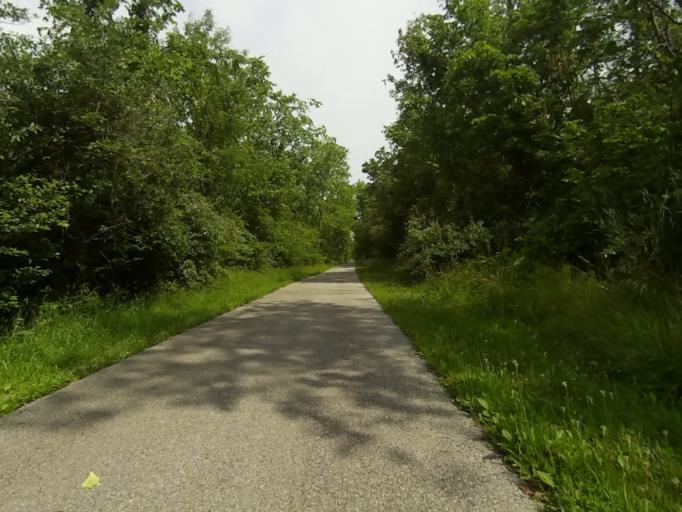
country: US
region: Ohio
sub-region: Summit County
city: Boston Heights
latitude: 41.2848
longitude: -81.5392
